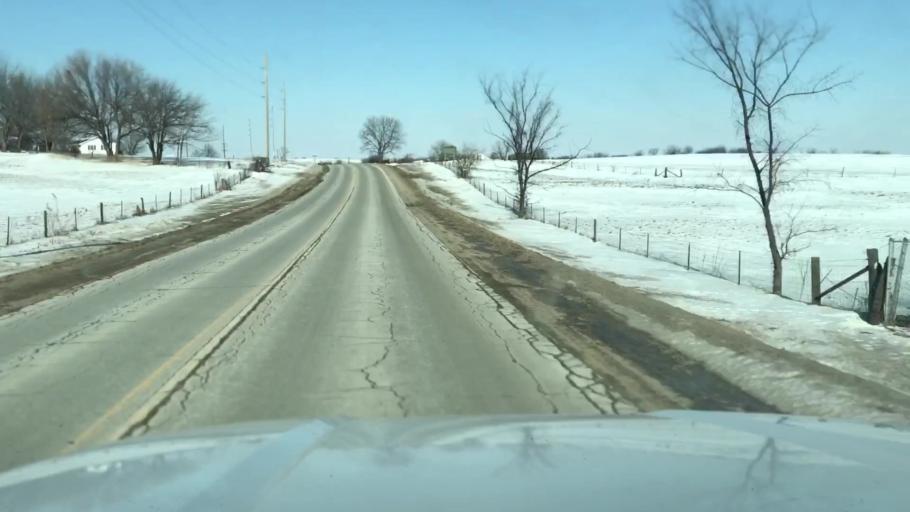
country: US
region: Missouri
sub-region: Andrew County
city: Savannah
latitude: 39.9555
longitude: -94.8491
